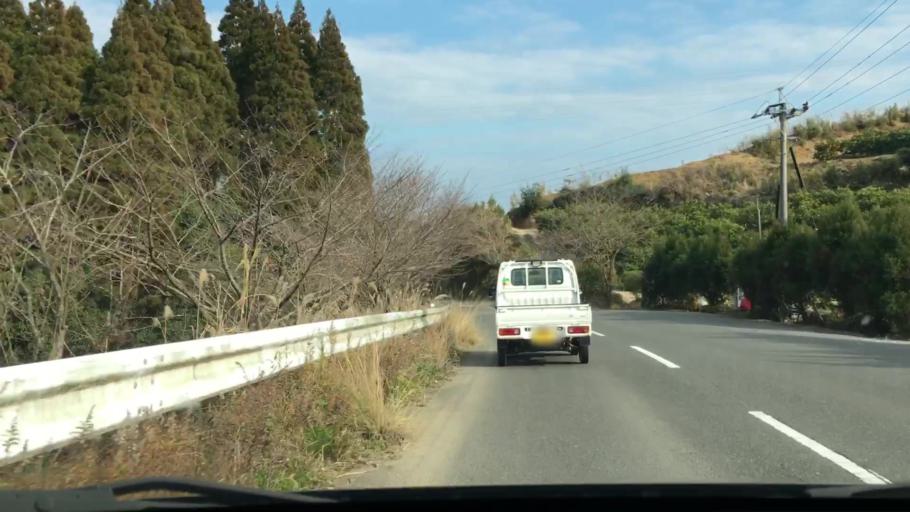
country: JP
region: Miyazaki
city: Nichinan
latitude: 31.5987
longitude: 131.3222
